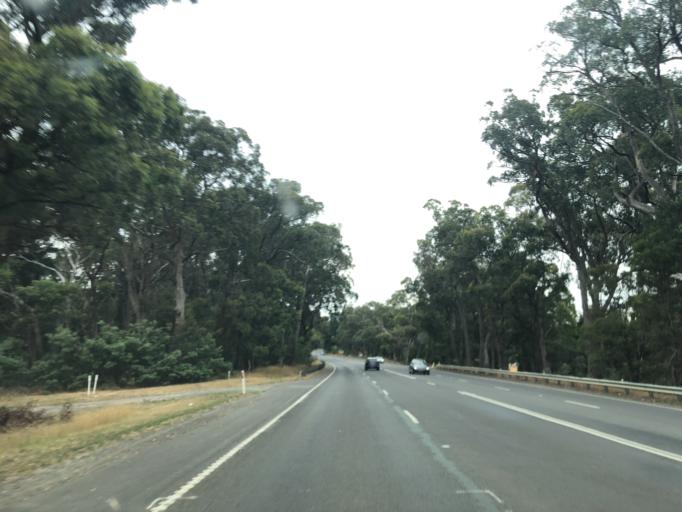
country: AU
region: Victoria
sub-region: Hume
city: Sunbury
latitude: -37.3759
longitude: 144.5266
